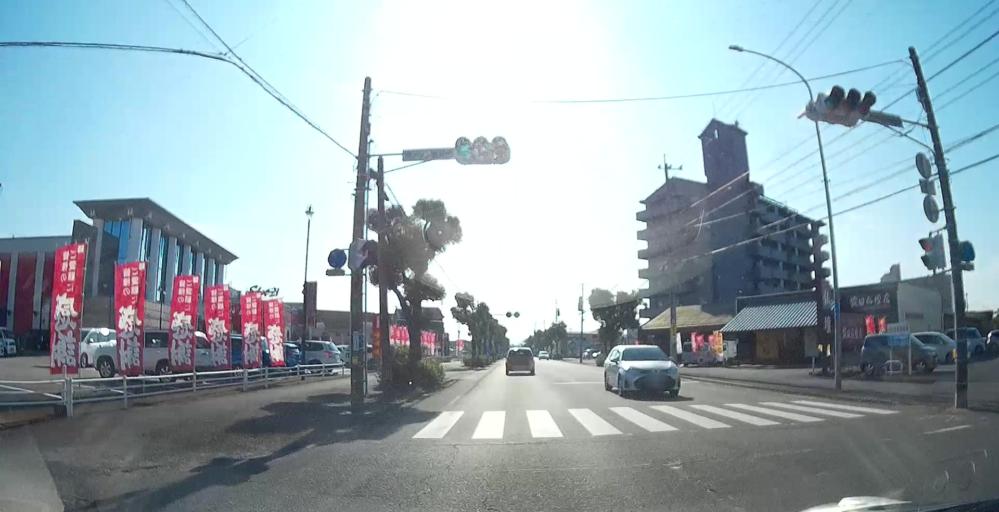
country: JP
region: Kumamoto
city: Kumamoto
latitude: 32.7511
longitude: 130.6860
